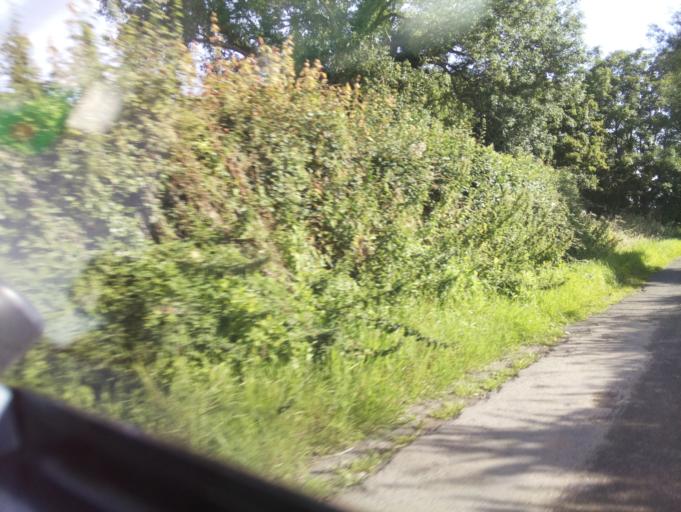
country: GB
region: England
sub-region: Bath and North East Somerset
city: Publow
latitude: 51.3990
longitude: -2.5310
